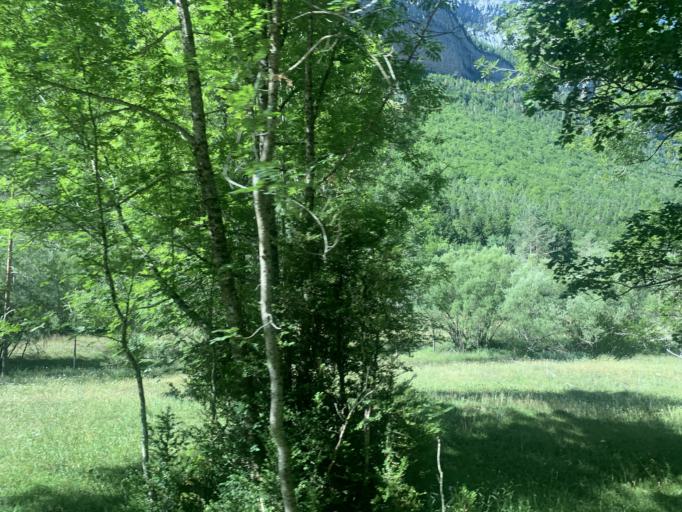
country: ES
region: Aragon
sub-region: Provincia de Huesca
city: Broto
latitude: 42.6501
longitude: -0.0653
